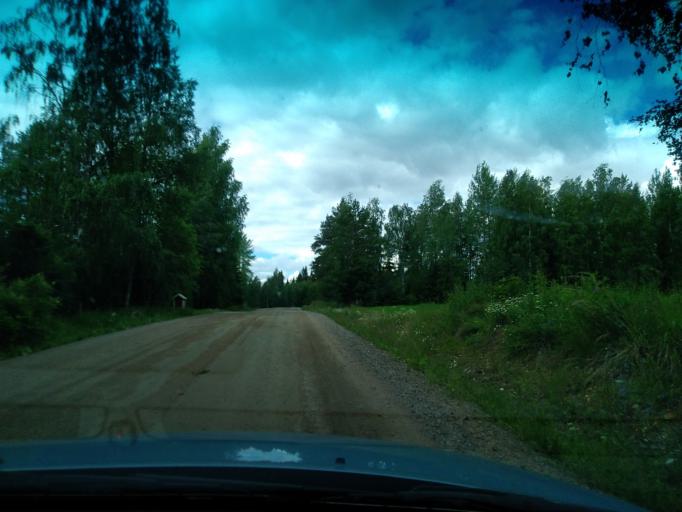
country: FI
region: Central Finland
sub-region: Saarijaervi-Viitasaari
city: Karstula
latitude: 62.8089
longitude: 25.0141
